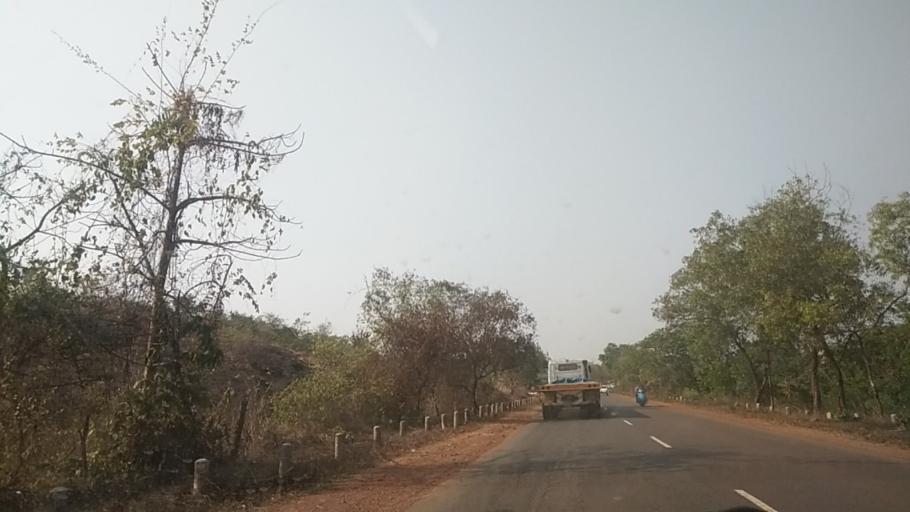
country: IN
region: Goa
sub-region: North Goa
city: Colovale
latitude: 15.6830
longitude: 73.8336
